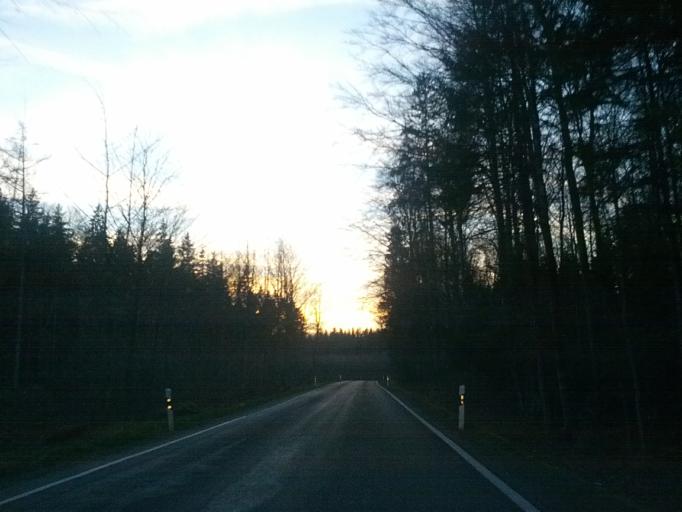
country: DE
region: Baden-Wuerttemberg
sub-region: Tuebingen Region
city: Aitrach
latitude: 47.9400
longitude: 10.0633
